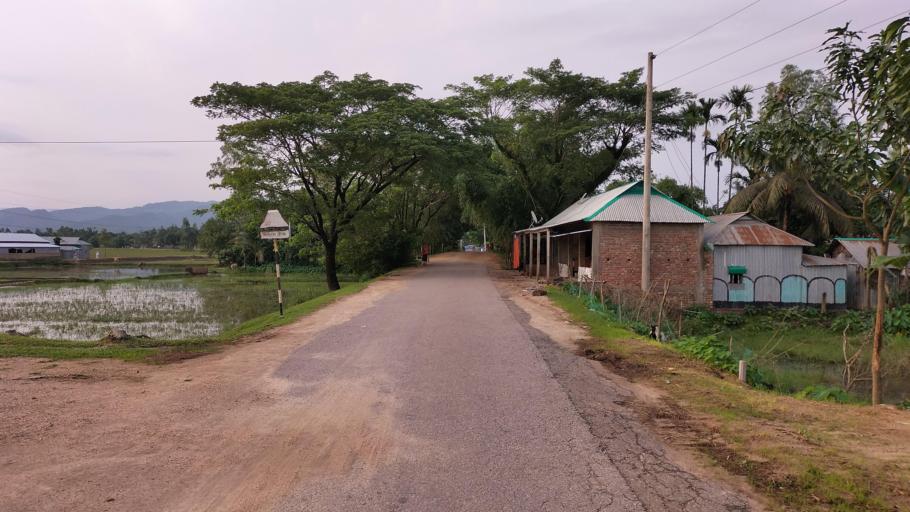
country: BD
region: Dhaka
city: Netrakona
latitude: 25.1328
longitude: 90.9134
